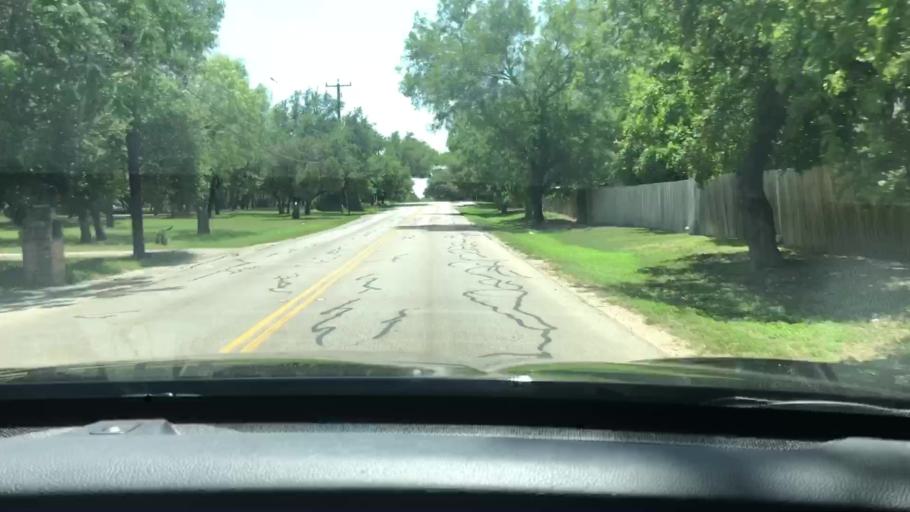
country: US
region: Texas
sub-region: Bexar County
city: Helotes
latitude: 29.5475
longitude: -98.6558
